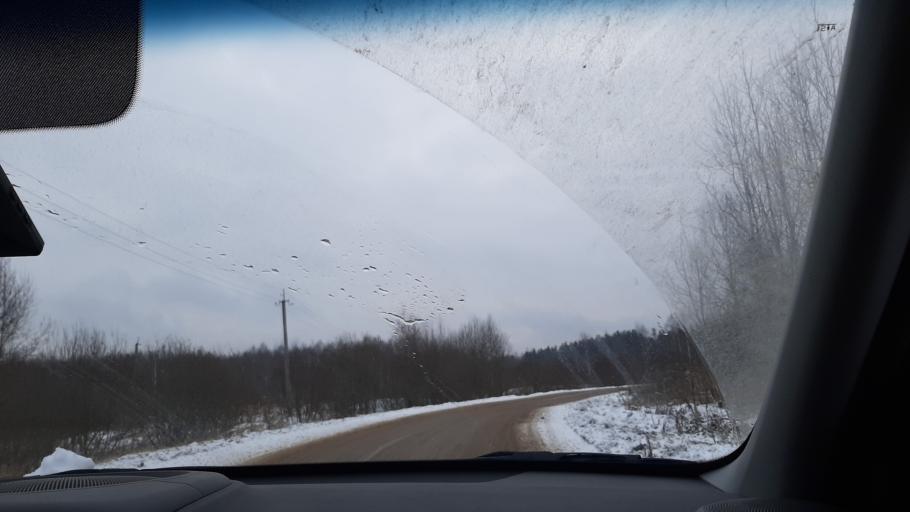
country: RU
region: Ivanovo
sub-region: Gorod Ivanovo
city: Ivanovo
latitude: 56.9246
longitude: 40.9824
